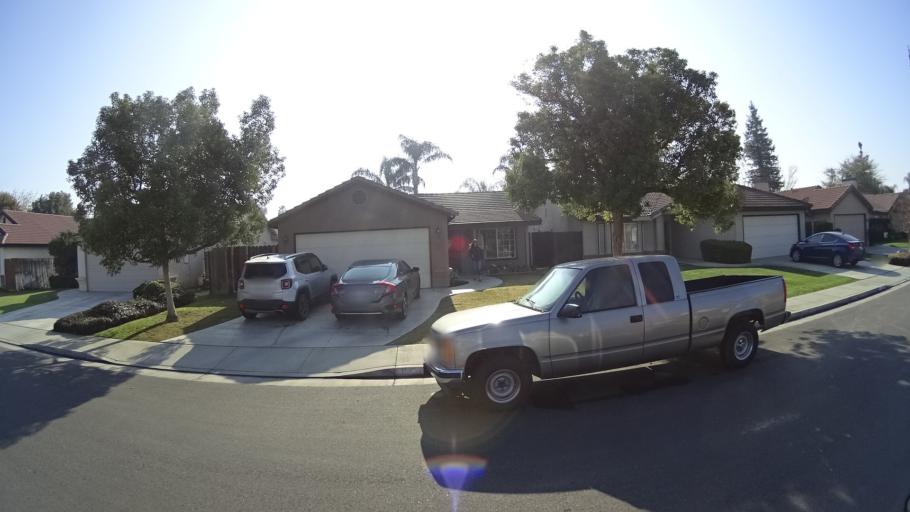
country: US
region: California
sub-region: Kern County
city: Greenacres
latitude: 35.3900
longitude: -119.1027
